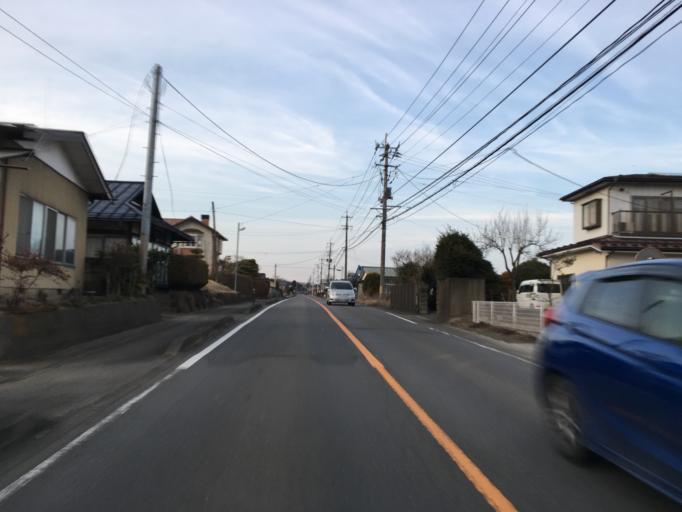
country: JP
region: Fukushima
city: Ishikawa
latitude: 36.9805
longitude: 140.3928
